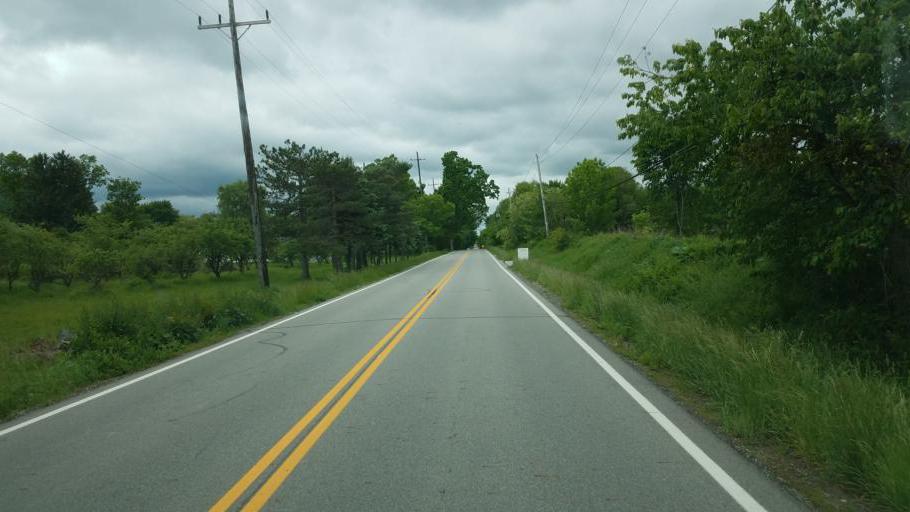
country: US
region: Ohio
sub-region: Geauga County
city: Burton
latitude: 41.3920
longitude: -81.1716
